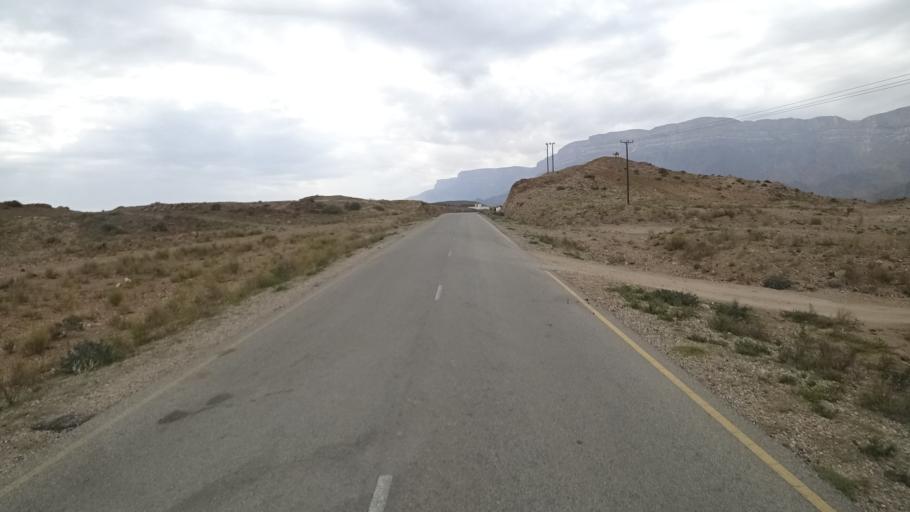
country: OM
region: Zufar
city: Salalah
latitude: 17.1622
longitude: 54.9870
